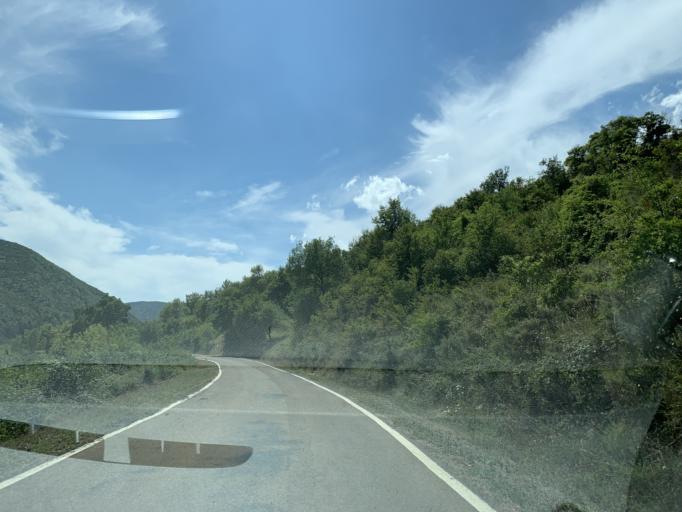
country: ES
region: Aragon
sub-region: Provincia de Huesca
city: Borau
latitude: 42.6335
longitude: -0.6471
